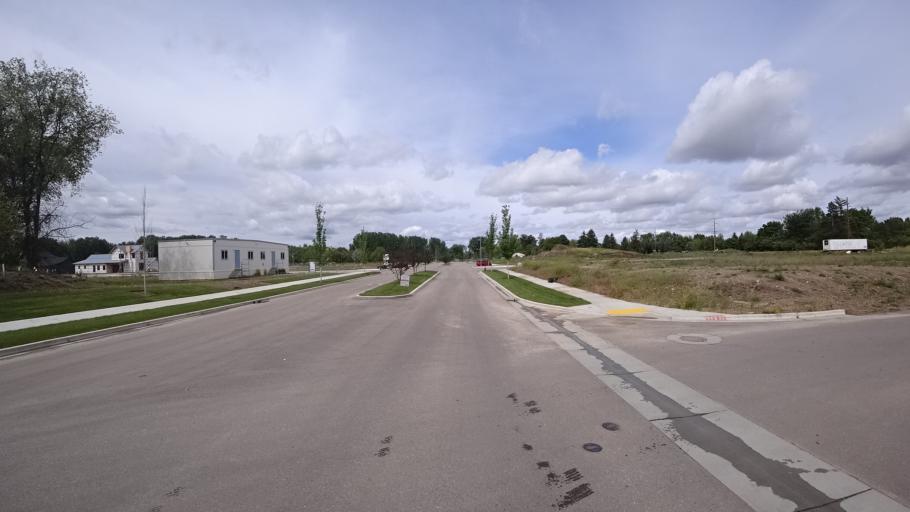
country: US
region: Idaho
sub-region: Ada County
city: Eagle
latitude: 43.6943
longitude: -116.3840
